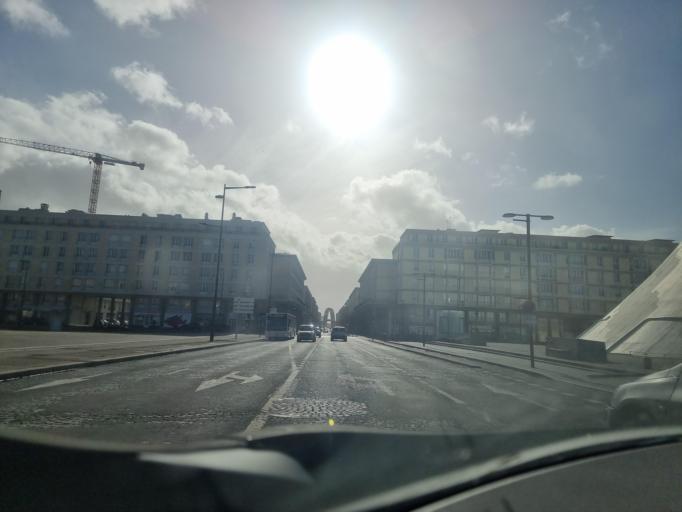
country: FR
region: Haute-Normandie
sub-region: Departement de la Seine-Maritime
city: Le Havre
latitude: 49.4907
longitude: 0.1077
